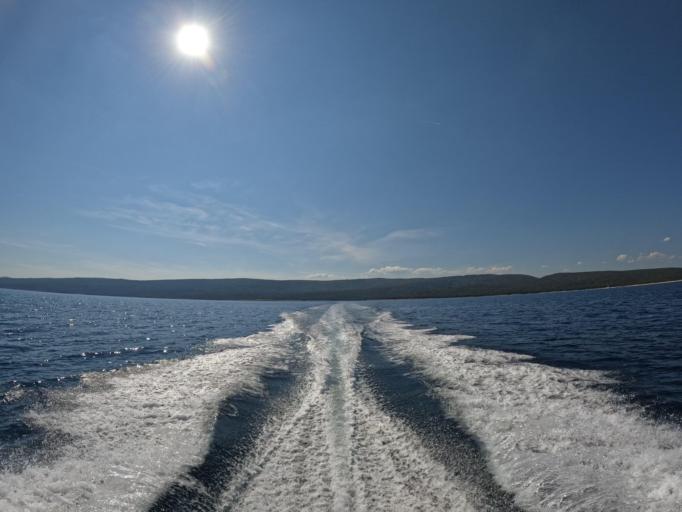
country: HR
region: Primorsko-Goranska
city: Cres
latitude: 44.9453
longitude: 14.4914
